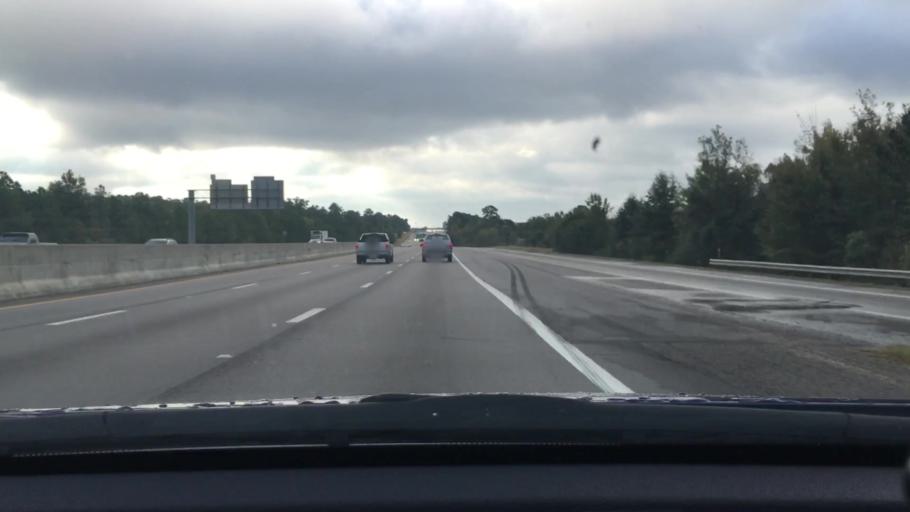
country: US
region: South Carolina
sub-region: Lexington County
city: Irmo
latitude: 34.0884
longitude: -81.1632
